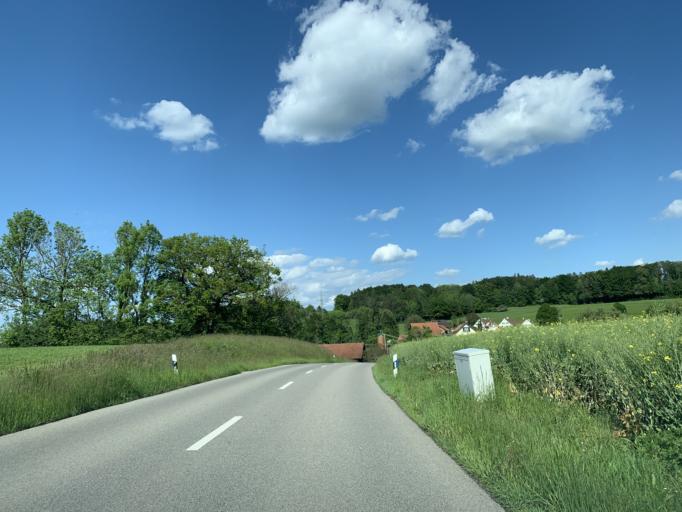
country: CH
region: Zurich
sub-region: Bezirk Pfaeffikon
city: Effretikon / Watt
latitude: 47.4424
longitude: 8.7232
